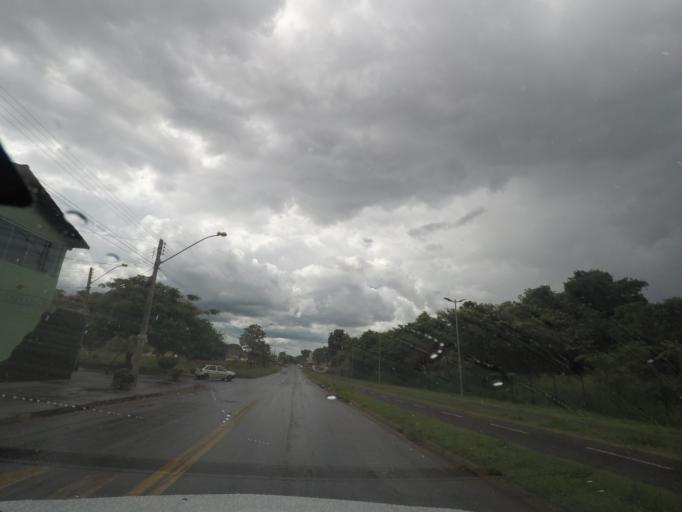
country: BR
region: Goias
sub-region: Goiania
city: Goiania
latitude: -16.7431
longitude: -49.3247
